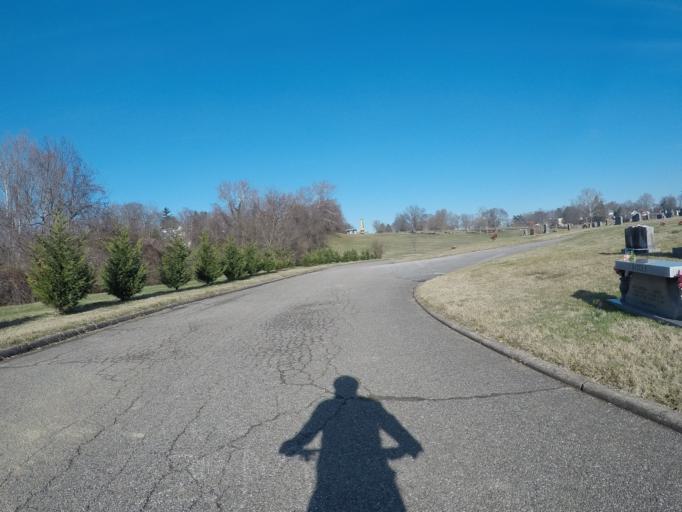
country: US
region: West Virginia
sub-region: Cabell County
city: Huntington
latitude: 38.4085
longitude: -82.4181
